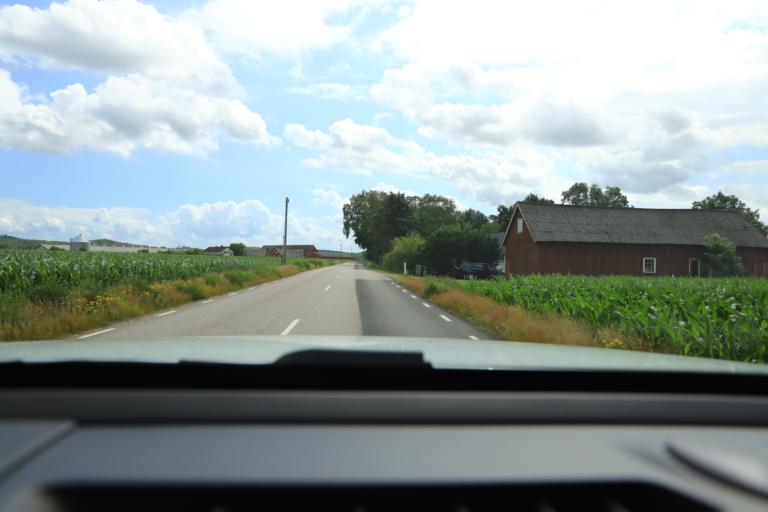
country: SE
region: Halland
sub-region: Varbergs Kommun
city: Tvaaker
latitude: 57.0402
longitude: 12.4348
